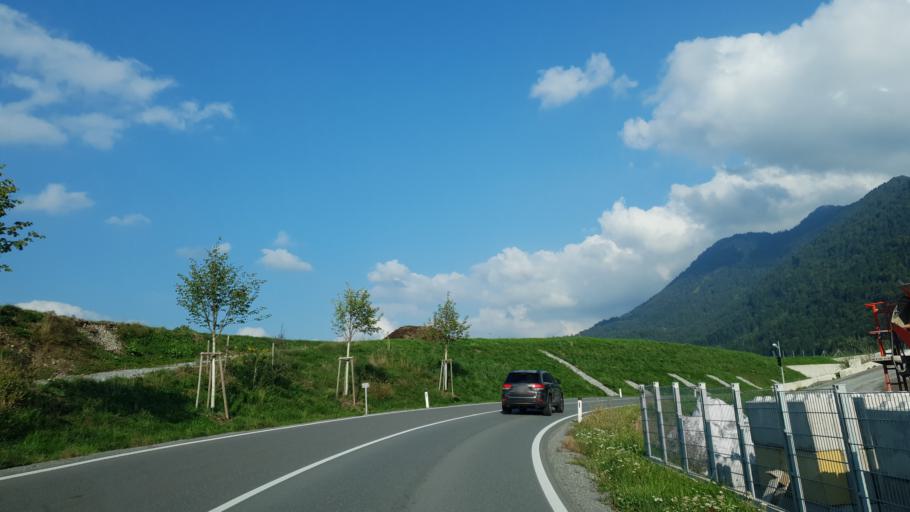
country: AT
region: Vorarlberg
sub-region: Politischer Bezirk Bregenz
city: Andelsbuch
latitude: 47.4054
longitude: 9.8799
